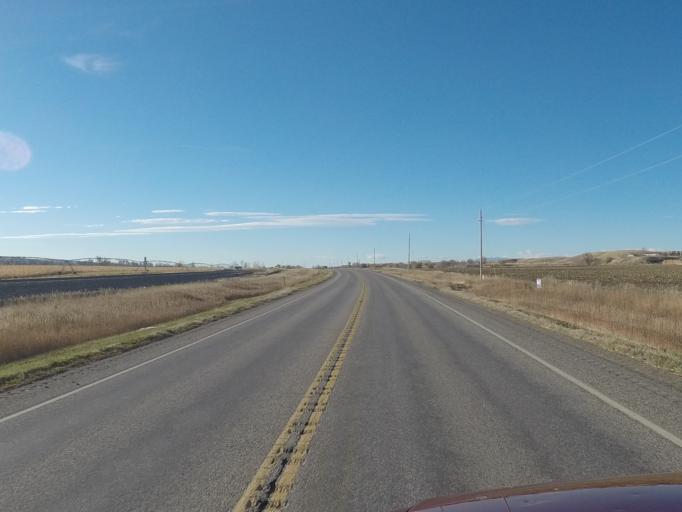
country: US
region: Montana
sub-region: Yellowstone County
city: Laurel
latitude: 45.5735
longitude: -108.8351
